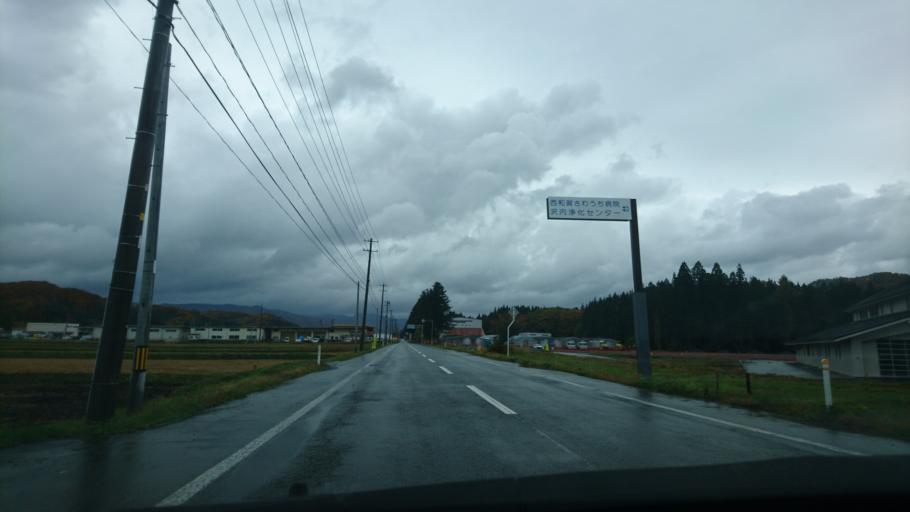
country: JP
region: Akita
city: Yokotemachi
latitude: 39.3714
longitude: 140.7607
